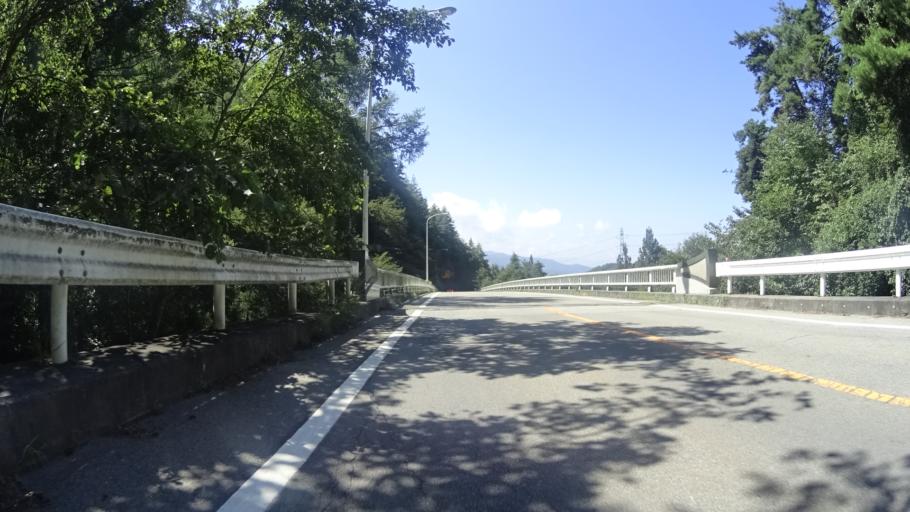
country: JP
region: Yamanashi
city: Enzan
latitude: 35.7525
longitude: 138.8105
